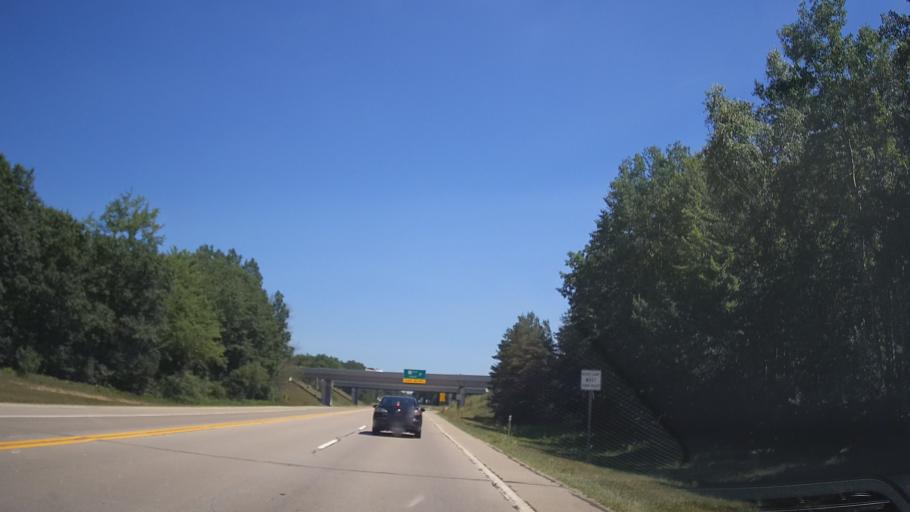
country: US
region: Michigan
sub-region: Clare County
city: Clare
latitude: 43.8662
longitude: -84.9126
